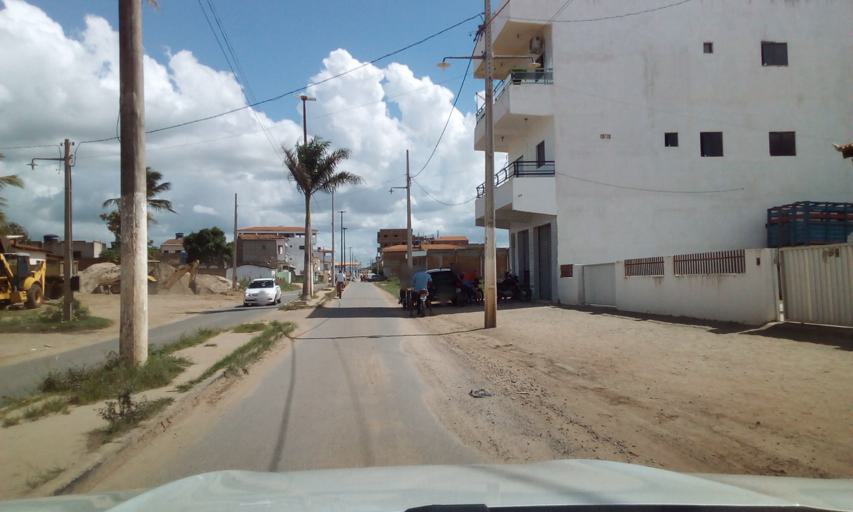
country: BR
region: Paraiba
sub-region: Guarabira
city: Guarabira
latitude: -6.8508
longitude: -35.3787
